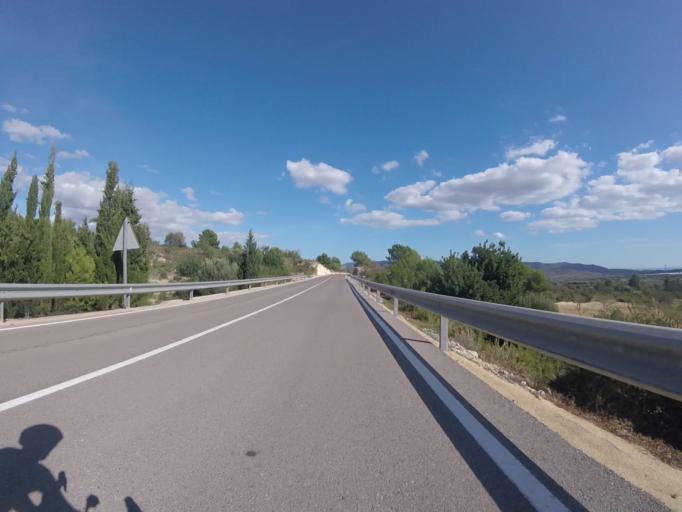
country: ES
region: Valencia
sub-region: Provincia de Castello
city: Alcala de Xivert
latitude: 40.3019
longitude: 0.1902
